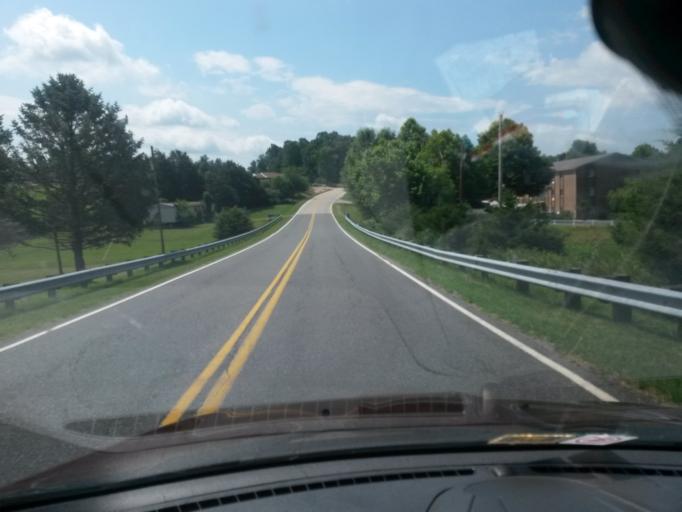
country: US
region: Virginia
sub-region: City of Buena Vista
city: Buena Vista
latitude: 37.9200
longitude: -79.2302
